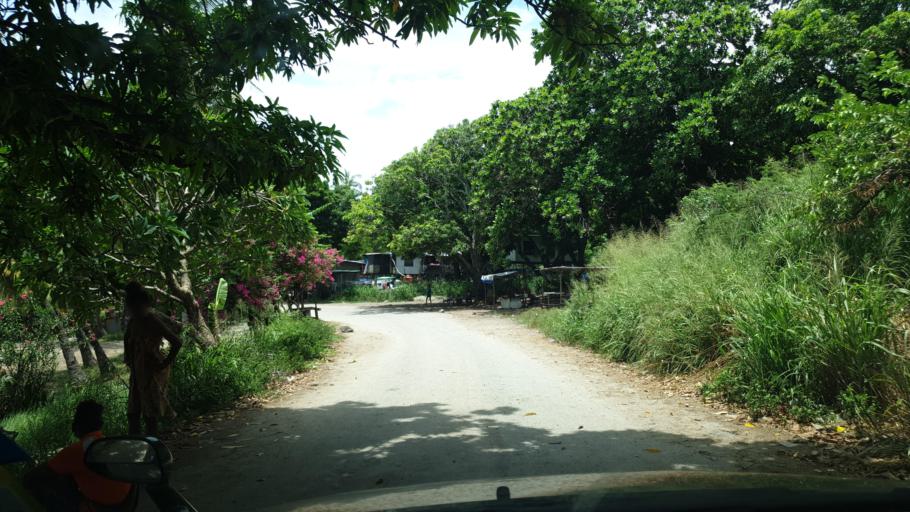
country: PG
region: National Capital
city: Port Moresby
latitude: -9.4205
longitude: 147.0463
